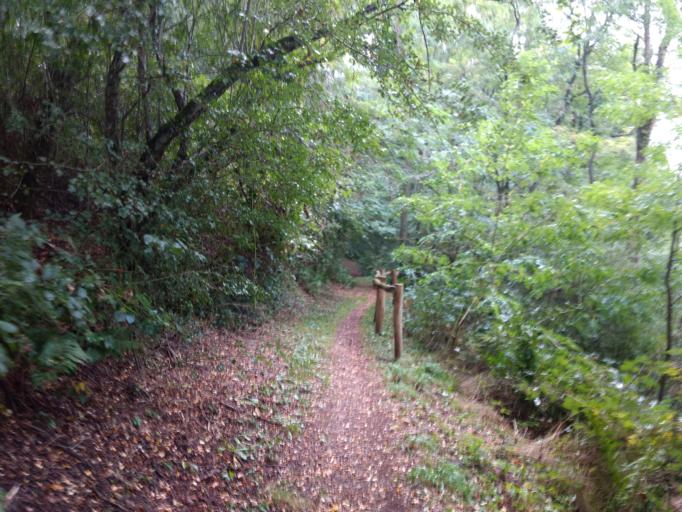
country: DE
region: Saarland
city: Nalbach
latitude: 49.3953
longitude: 6.8028
